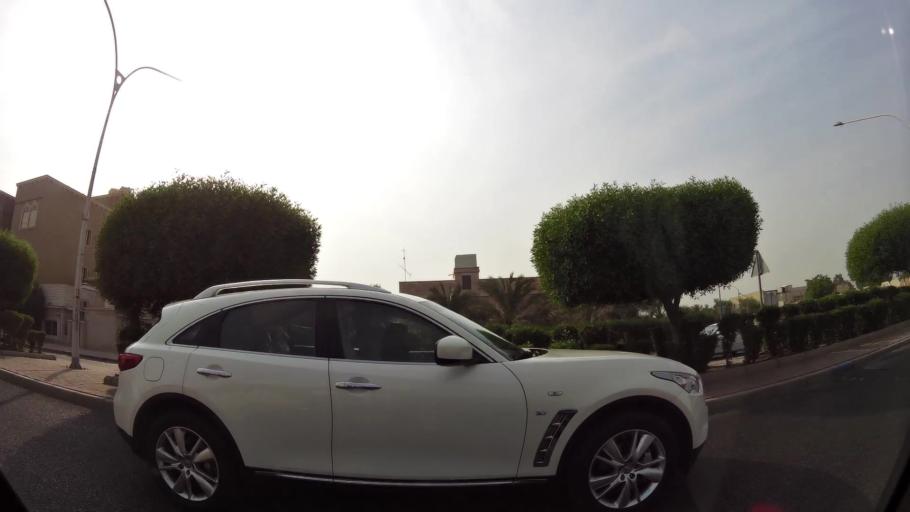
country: KW
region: Al Farwaniyah
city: Al Farwaniyah
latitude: 29.2953
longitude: 47.9538
